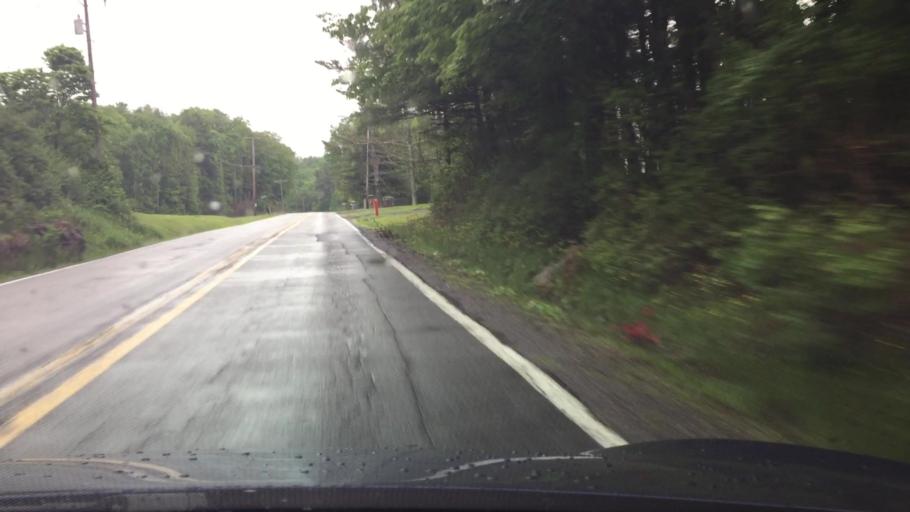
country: US
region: West Virginia
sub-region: Raleigh County
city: Shady Spring
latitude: 37.6898
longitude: -81.0614
